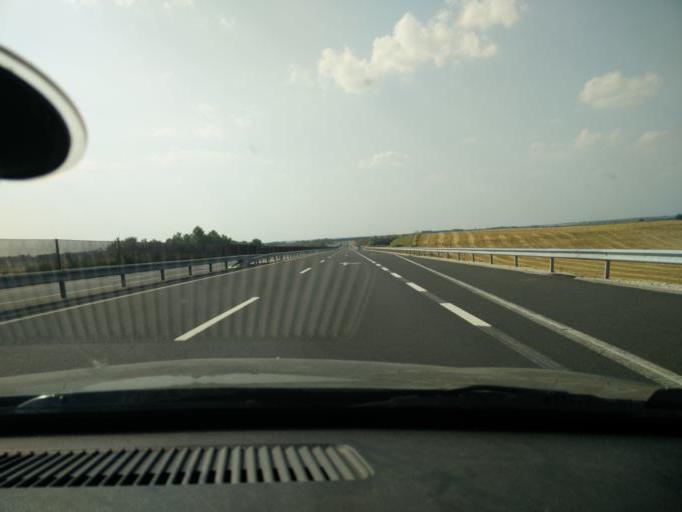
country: HU
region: Tolna
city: Tolna
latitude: 46.4057
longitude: 18.7425
